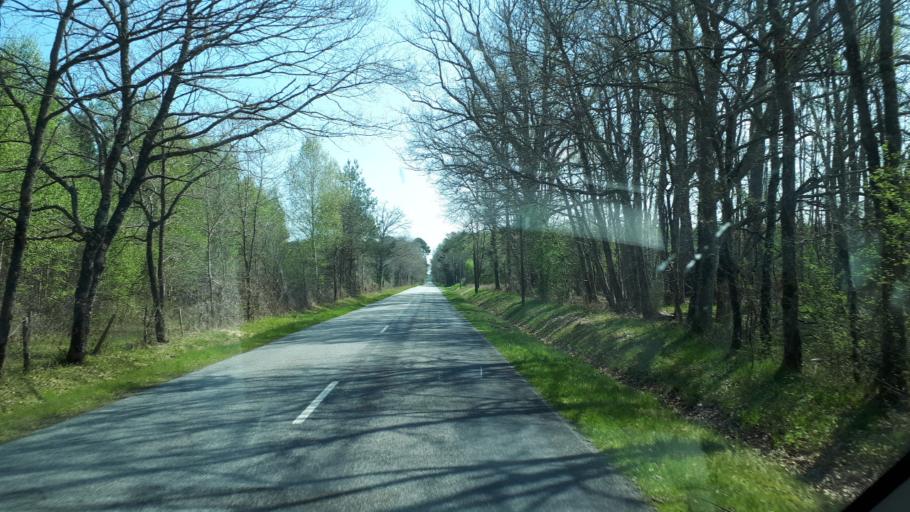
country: FR
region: Centre
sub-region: Departement du Loir-et-Cher
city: Theillay
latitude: 47.3138
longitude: 2.0666
